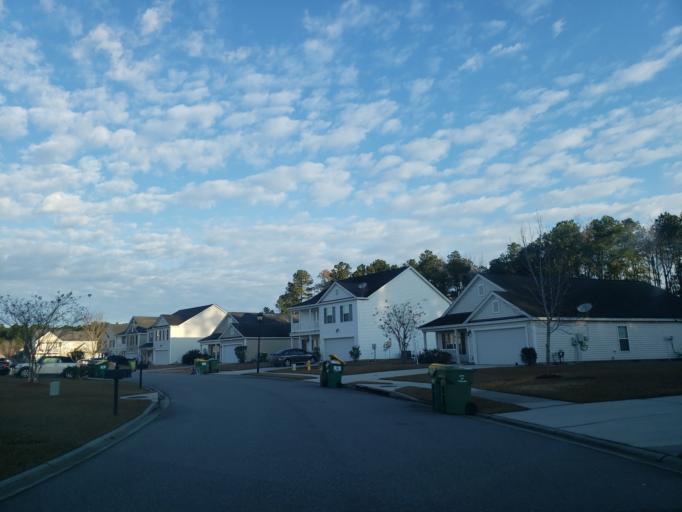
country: US
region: Georgia
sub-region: Chatham County
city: Bloomingdale
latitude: 32.1528
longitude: -81.2695
